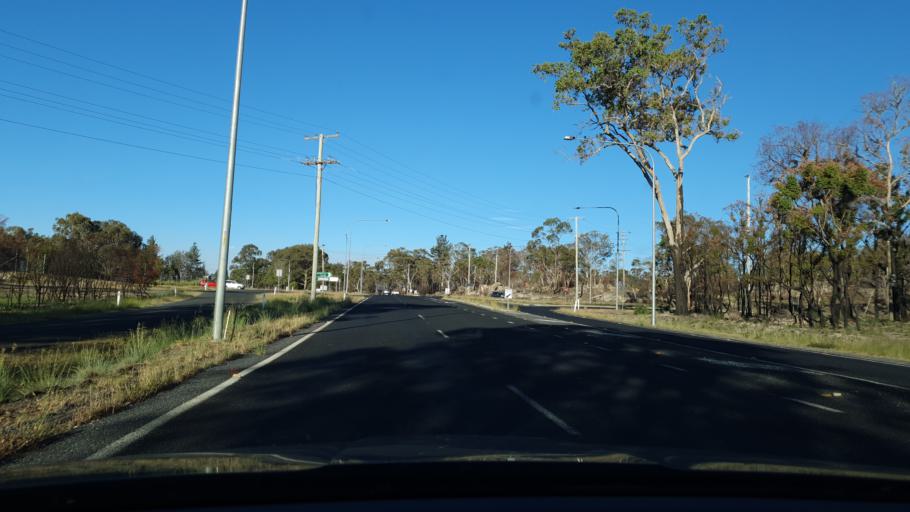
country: AU
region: Queensland
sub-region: Southern Downs
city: Stanthorpe
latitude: -28.6363
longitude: 151.9497
